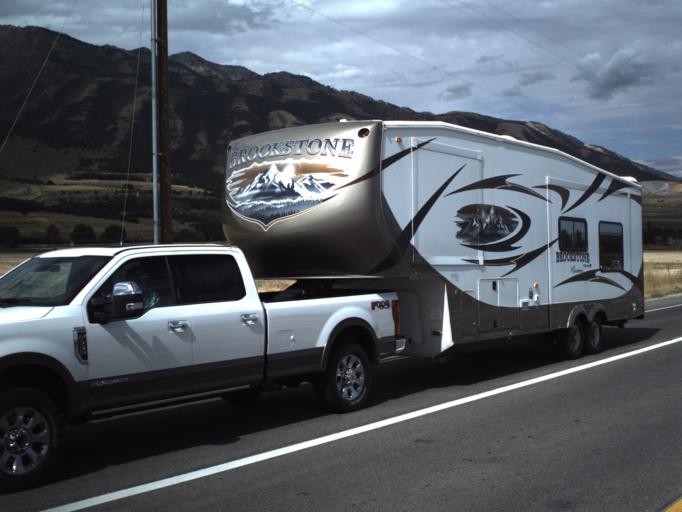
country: US
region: Utah
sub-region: Cache County
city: Wellsville
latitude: 41.6163
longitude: -111.9335
